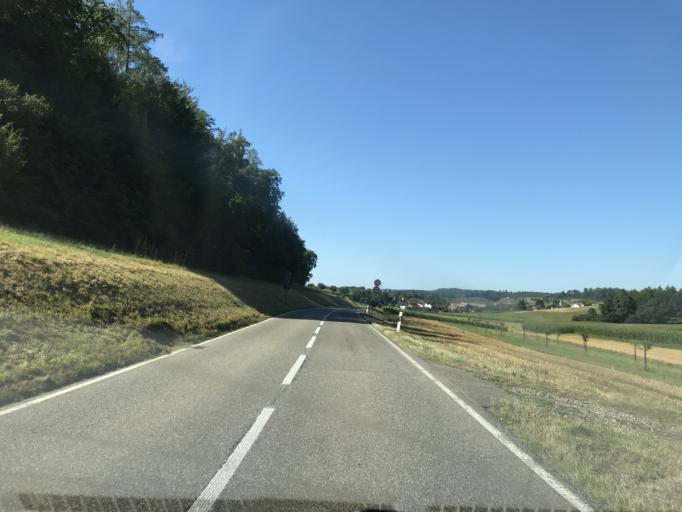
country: DE
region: Baden-Wuerttemberg
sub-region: Freiburg Region
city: Rheinfelden (Baden)
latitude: 47.6005
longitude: 7.8052
